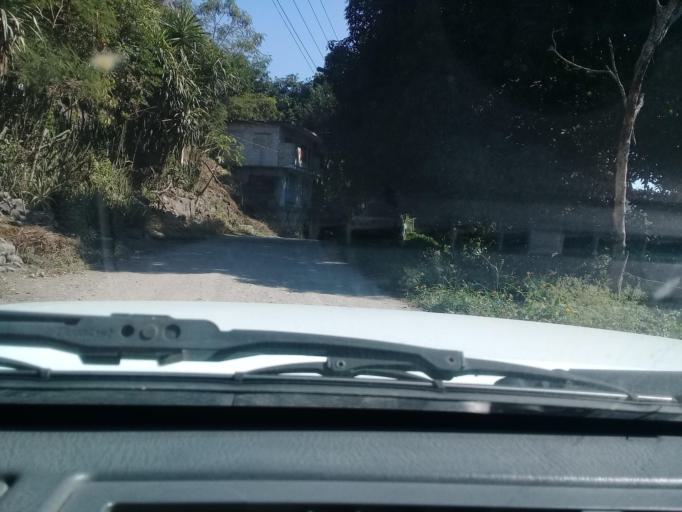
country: MX
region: Veracruz
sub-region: Emiliano Zapata
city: Plan del Rio
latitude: 19.4265
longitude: -96.6153
